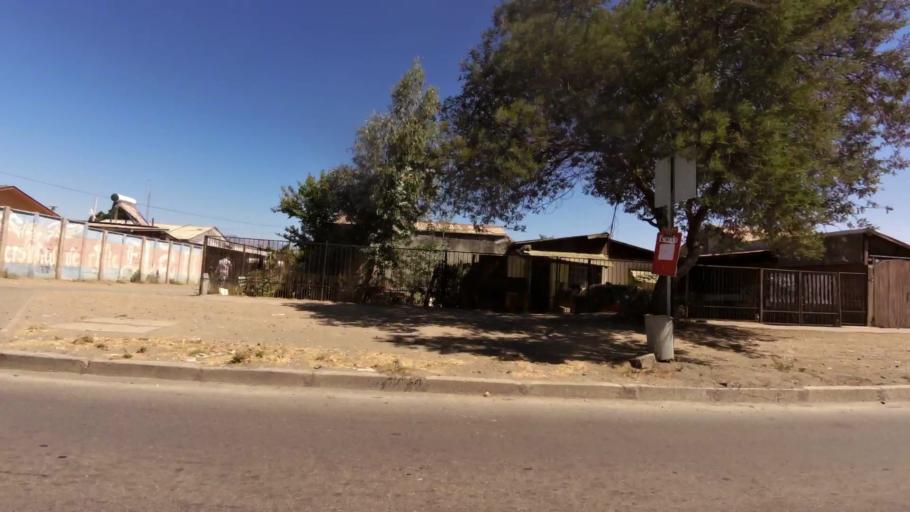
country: CL
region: O'Higgins
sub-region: Provincia de Cachapoal
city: Rancagua
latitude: -34.1667
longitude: -70.7108
